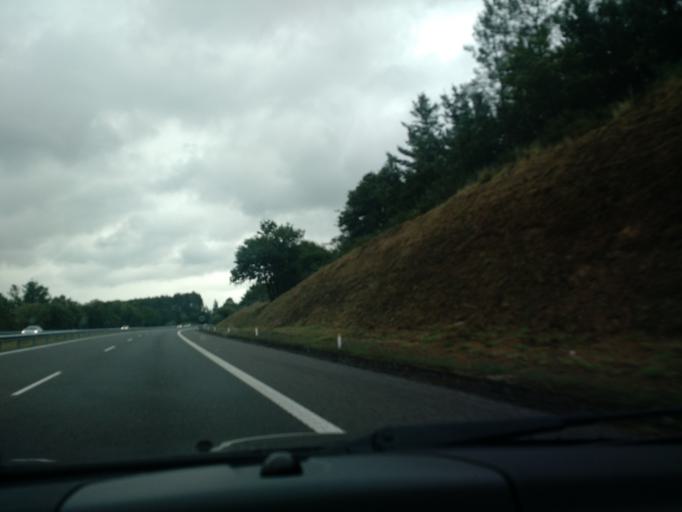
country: ES
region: Galicia
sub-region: Provincia da Coruna
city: Ordes
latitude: 43.0295
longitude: -8.4001
